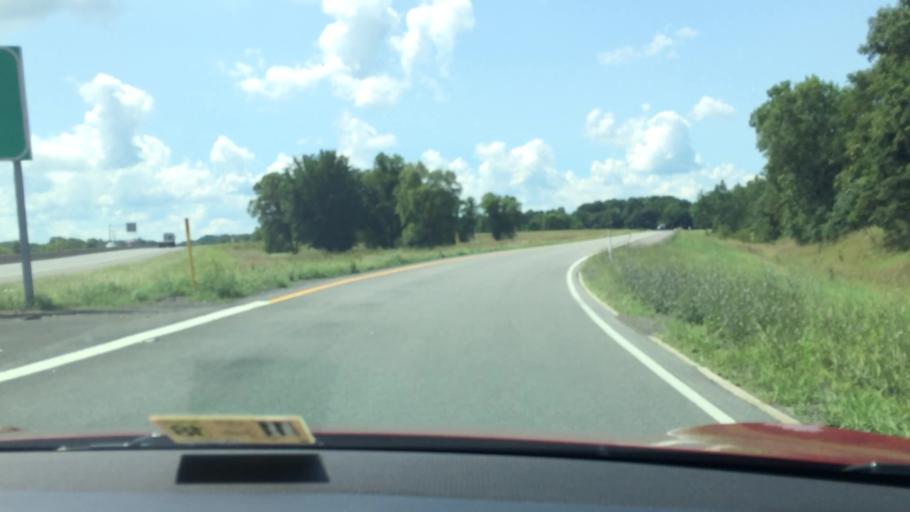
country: US
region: Indiana
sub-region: Saint Joseph County
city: South Bend
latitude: 41.6753
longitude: -86.3411
